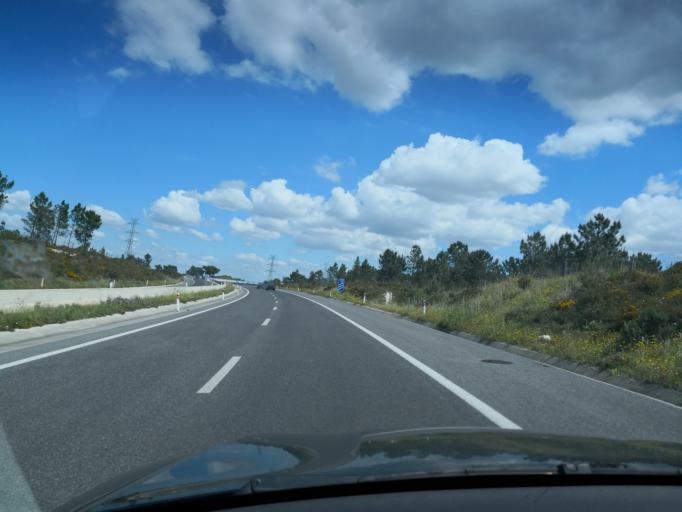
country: PT
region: Setubal
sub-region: Seixal
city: Amora
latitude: 38.6060
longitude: -9.1439
